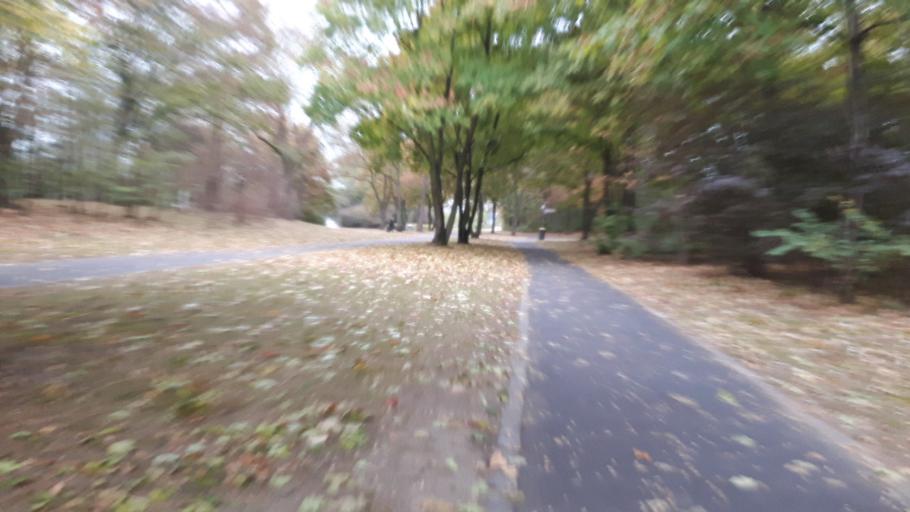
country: DE
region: North Rhine-Westphalia
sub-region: Regierungsbezirk Koln
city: Bonn
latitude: 50.7203
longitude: 7.1424
